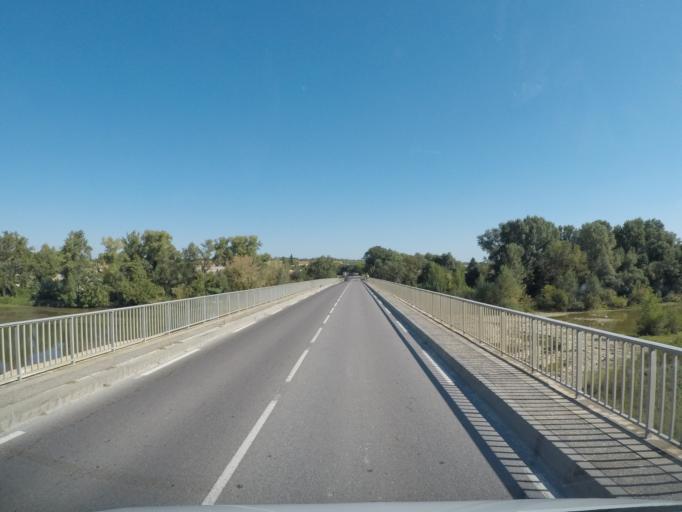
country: FR
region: Languedoc-Roussillon
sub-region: Departement du Gard
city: Moussac
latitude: 43.9772
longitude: 4.2284
